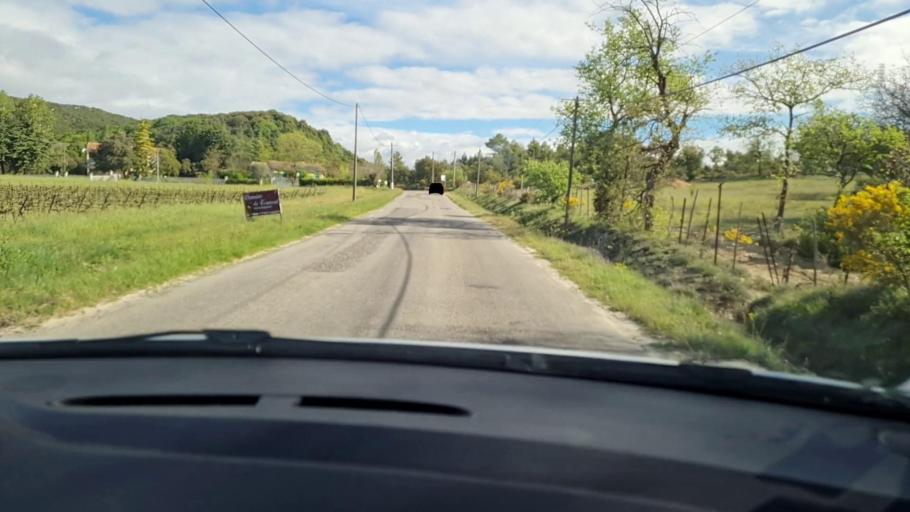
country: FR
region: Languedoc-Roussillon
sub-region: Departement du Gard
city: Sauve
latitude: 43.9666
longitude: 3.9474
